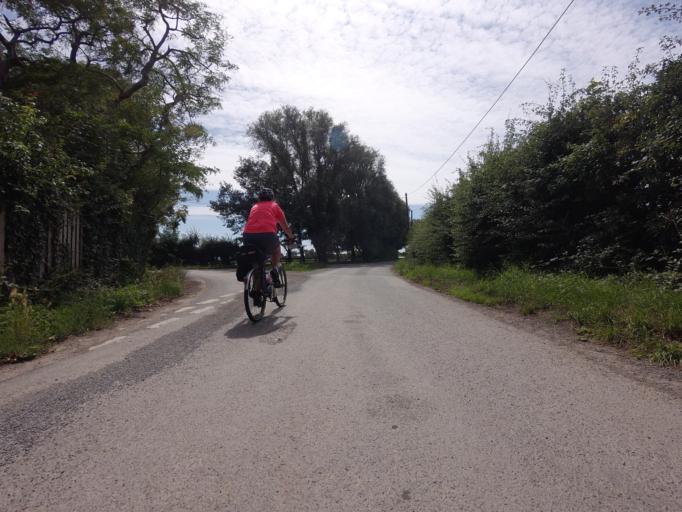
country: GB
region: England
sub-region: Kent
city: Stone
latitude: 50.9941
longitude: 0.8059
